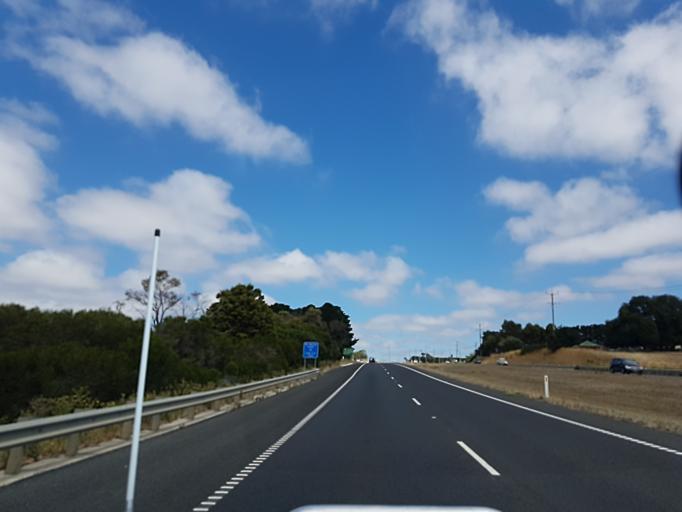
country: AU
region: Victoria
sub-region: Greater Geelong
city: Wandana Heights
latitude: -38.2126
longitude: 144.1858
